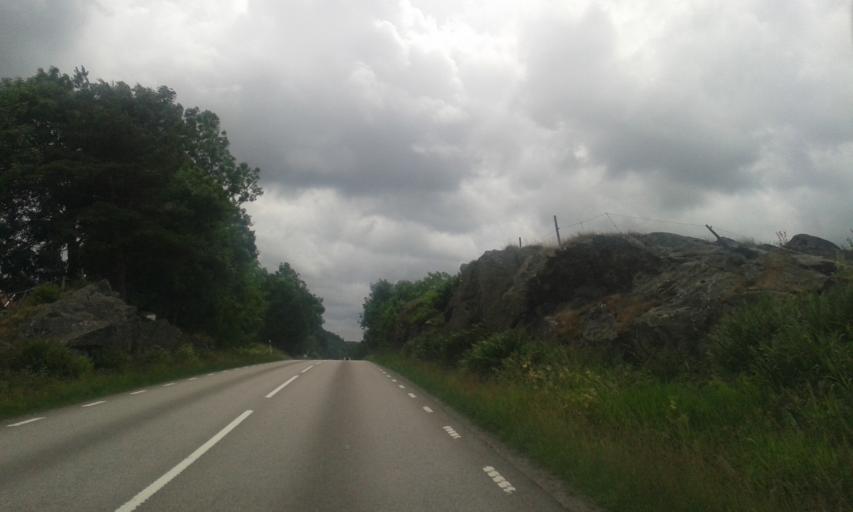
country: SE
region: Vaestra Goetaland
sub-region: Kungalvs Kommun
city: Kode
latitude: 57.8758
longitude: 11.9015
